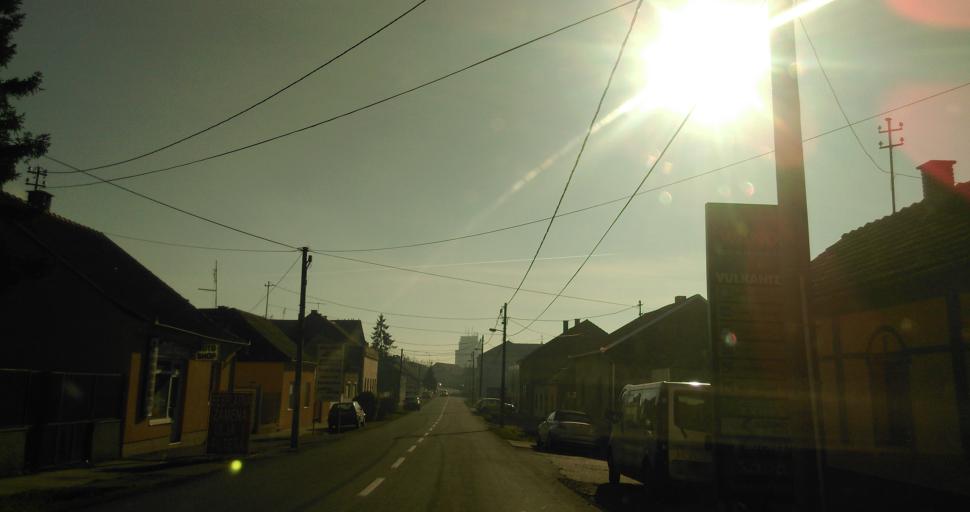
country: RS
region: Autonomna Pokrajina Vojvodina
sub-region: Sremski Okrug
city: Ruma
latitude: 45.0095
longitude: 19.8316
